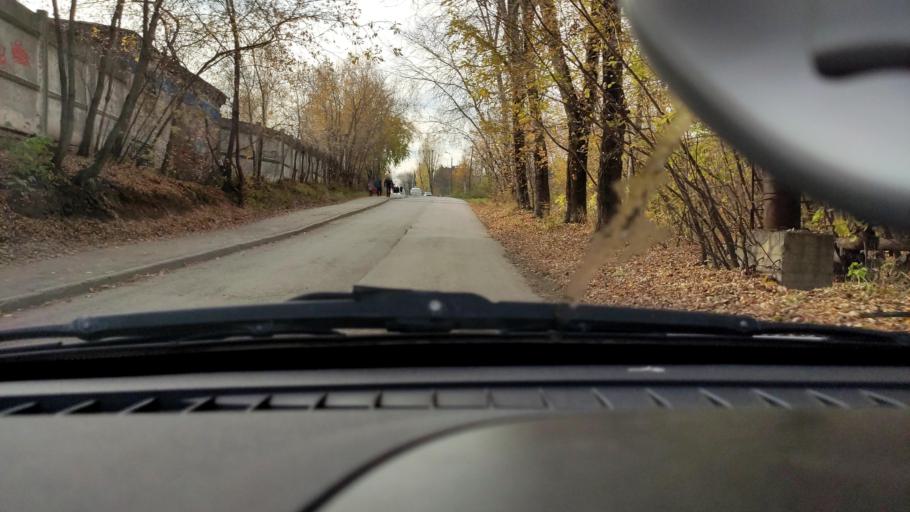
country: RU
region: Perm
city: Polazna
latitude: 58.1237
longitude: 56.3827
